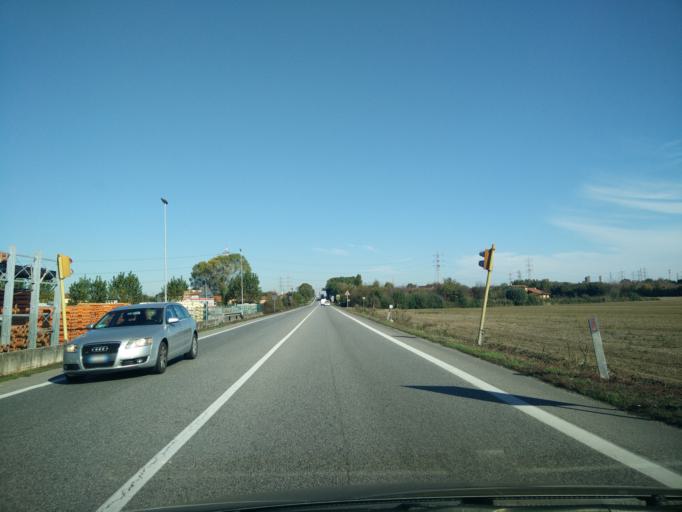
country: IT
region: Veneto
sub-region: Provincia di Venezia
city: Fornase
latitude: 45.4363
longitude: 12.1944
